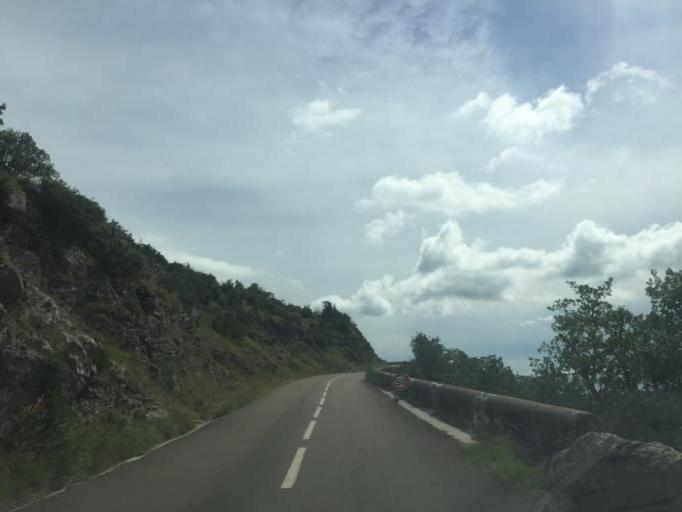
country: FR
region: Rhone-Alpes
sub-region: Departement de l'Ardeche
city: Villeneuve-de-Berg
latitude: 44.6257
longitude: 4.5455
